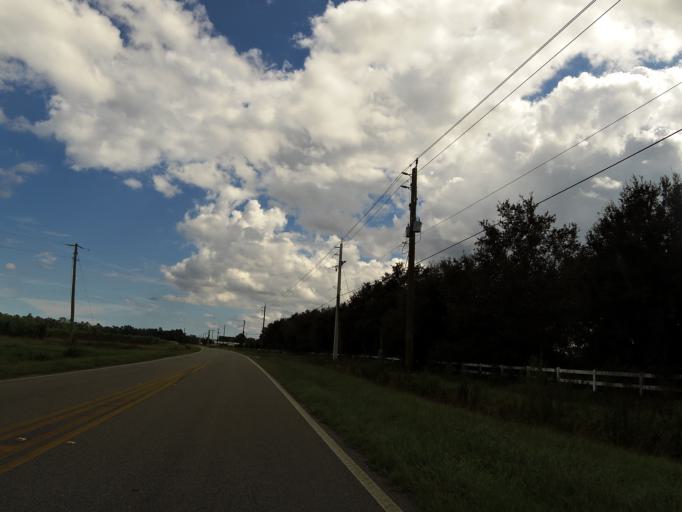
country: US
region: Florida
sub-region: Saint Johns County
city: Saint Augustine South
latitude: 29.8277
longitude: -81.4938
